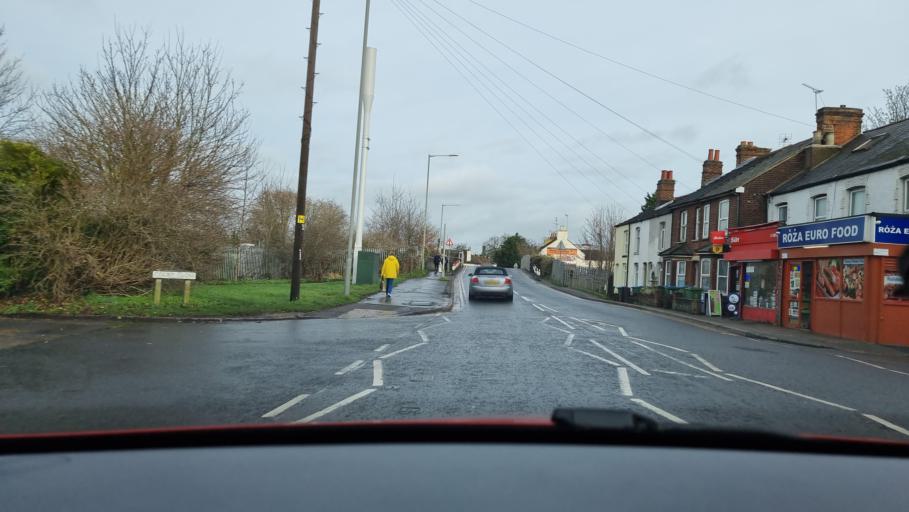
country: GB
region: England
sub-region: Buckinghamshire
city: Aylesbury
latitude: 51.8091
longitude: -0.8085
